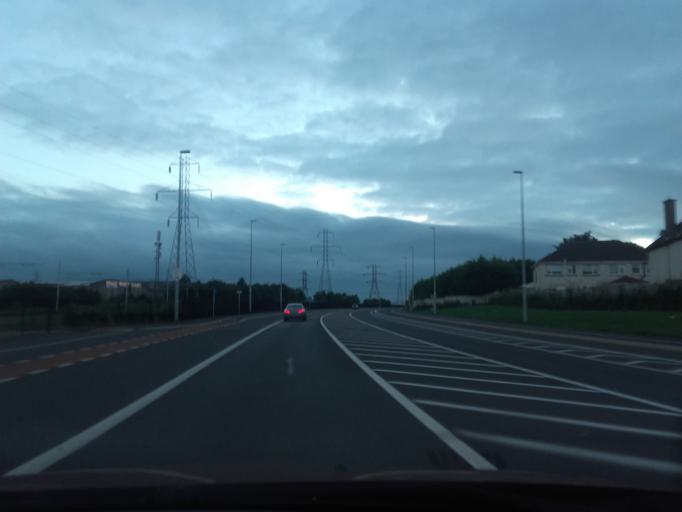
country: IE
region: Leinster
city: Tallaght
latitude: 53.2984
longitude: -6.3768
